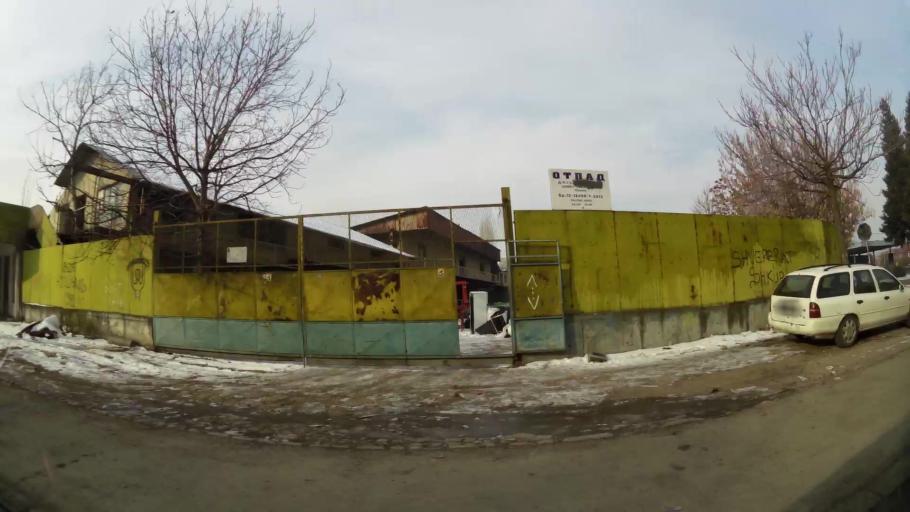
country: MK
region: Cair
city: Cair
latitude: 42.0173
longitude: 21.4310
